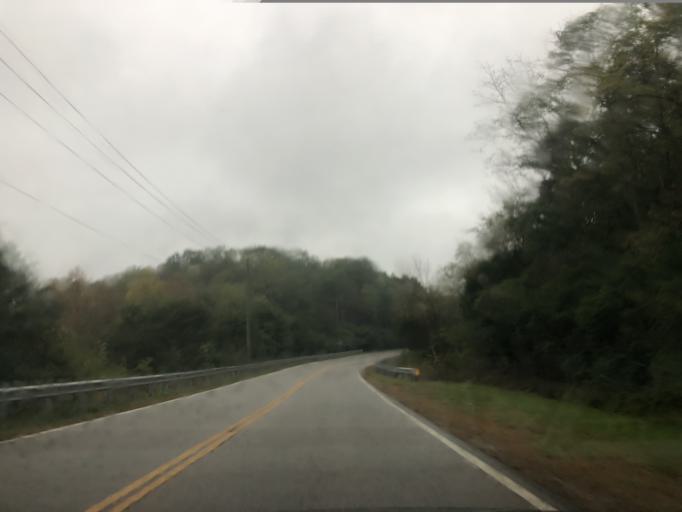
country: US
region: Ohio
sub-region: Hamilton County
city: The Village of Indian Hill
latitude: 39.2241
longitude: -84.2744
